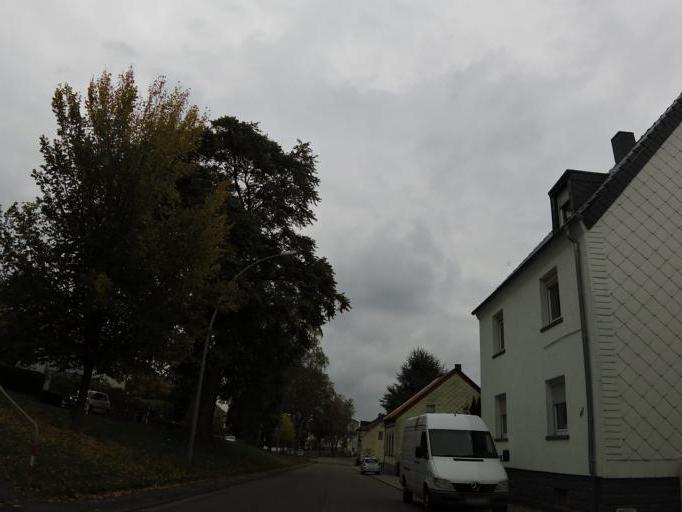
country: DE
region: Saarland
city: Sankt Ingbert
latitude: 49.2687
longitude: 7.1066
